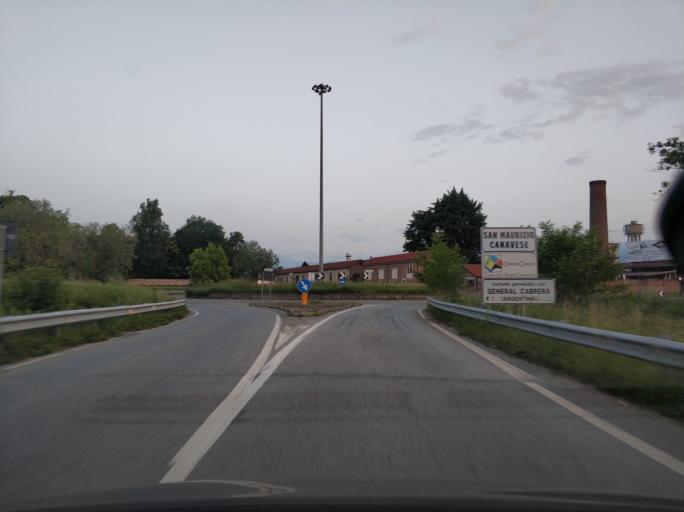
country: IT
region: Piedmont
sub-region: Provincia di Torino
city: San Maurizio
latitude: 45.2178
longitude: 7.6402
